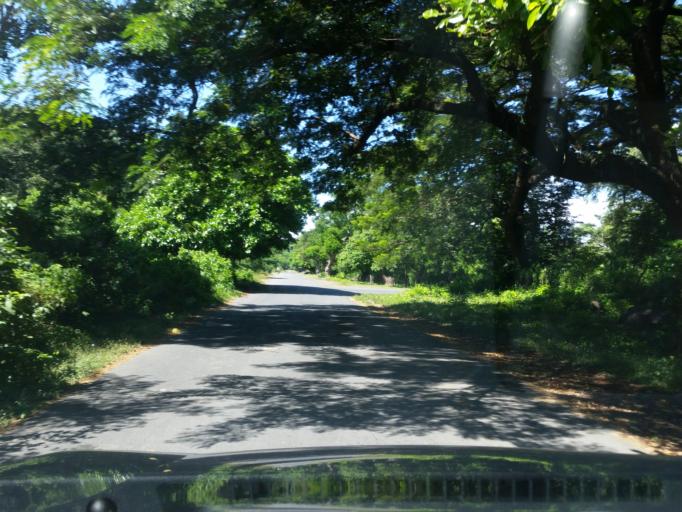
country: NI
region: Granada
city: Granada
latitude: 11.9040
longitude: -85.9350
